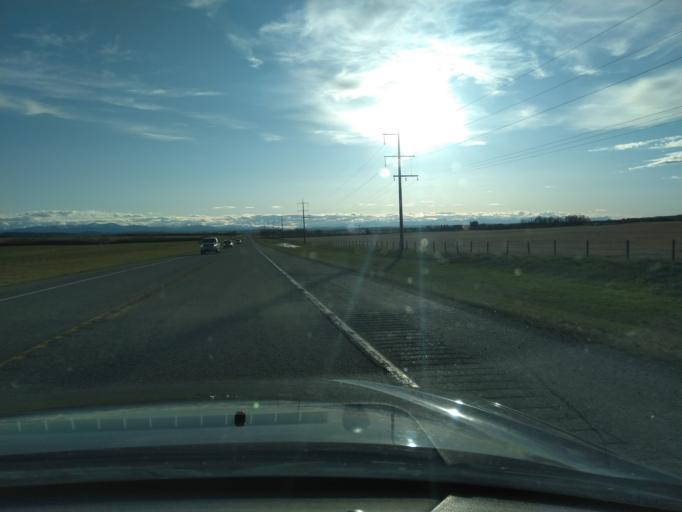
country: CA
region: Alberta
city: Cochrane
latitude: 51.0235
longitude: -114.3416
